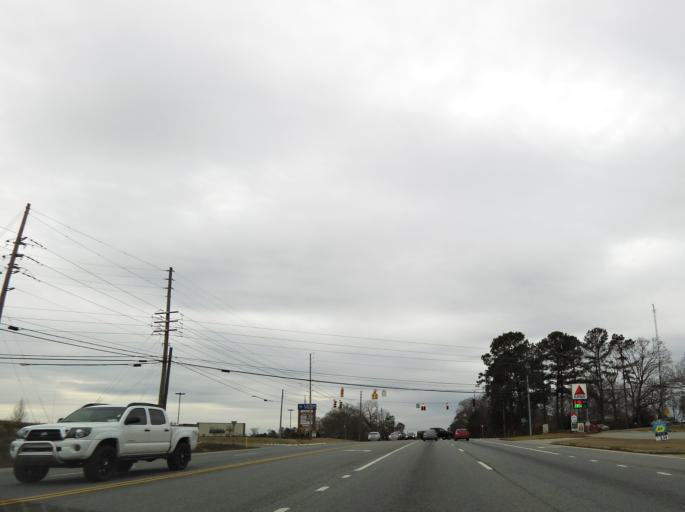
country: US
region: Georgia
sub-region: Houston County
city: Robins Air Force Base
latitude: 32.5689
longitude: -83.5941
